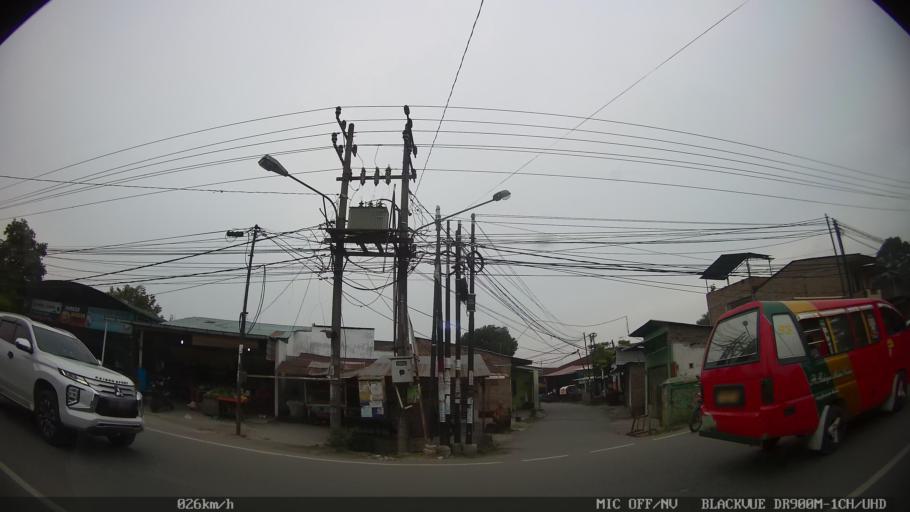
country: ID
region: North Sumatra
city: Deli Tua
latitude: 3.5433
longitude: 98.7176
